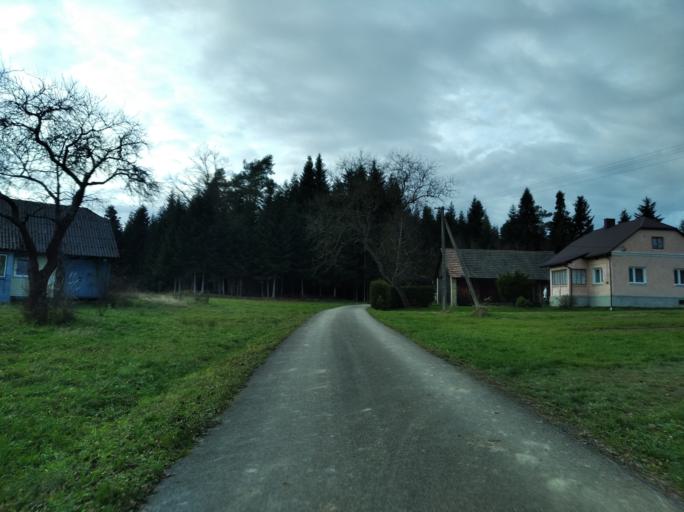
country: PL
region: Subcarpathian Voivodeship
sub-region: Powiat brzozowski
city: Domaradz
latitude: 49.7824
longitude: 21.9124
